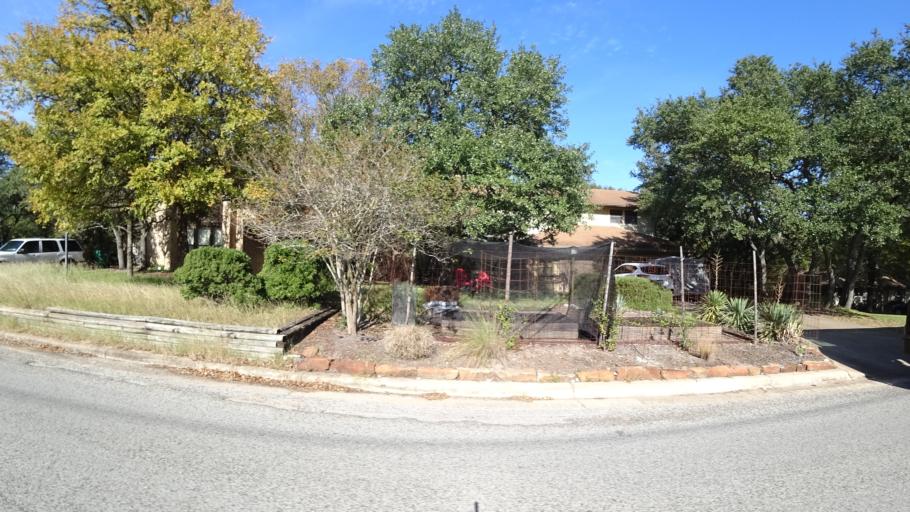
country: US
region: Texas
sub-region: Travis County
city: Shady Hollow
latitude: 30.2221
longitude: -97.9102
